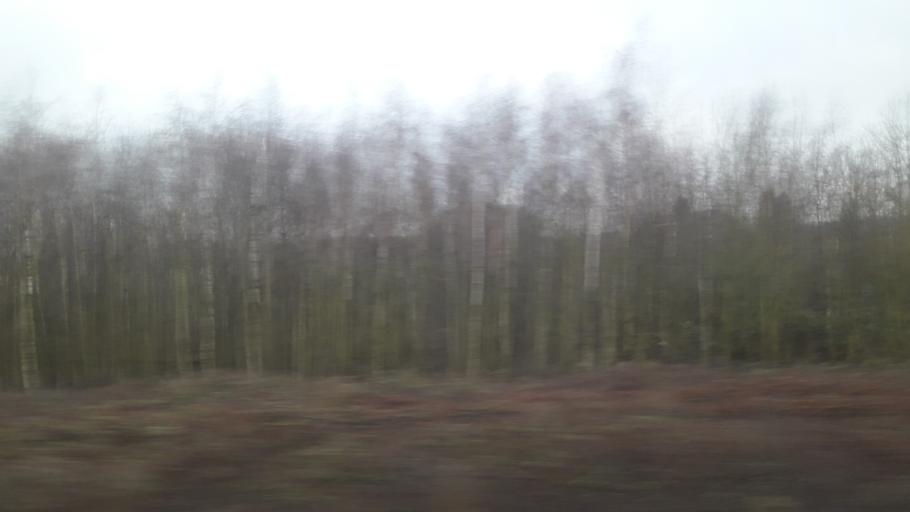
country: DE
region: North Rhine-Westphalia
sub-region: Regierungsbezirk Arnsberg
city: Bonen
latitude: 51.6172
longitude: 7.7464
